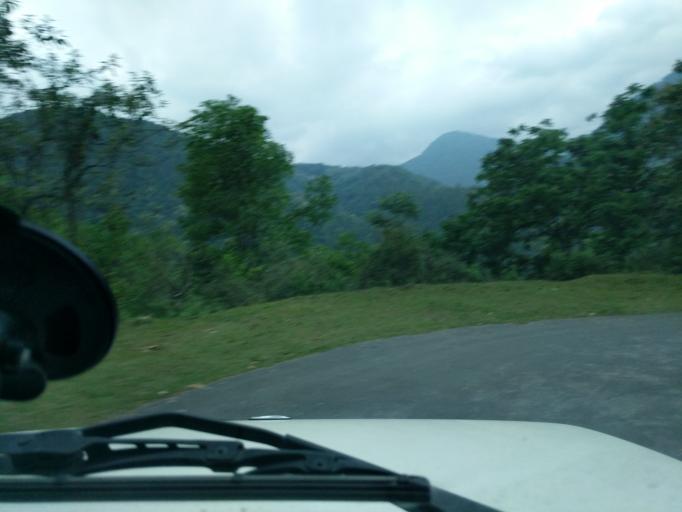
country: BT
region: Mongar
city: Mongar
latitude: 27.2872
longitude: 91.1495
